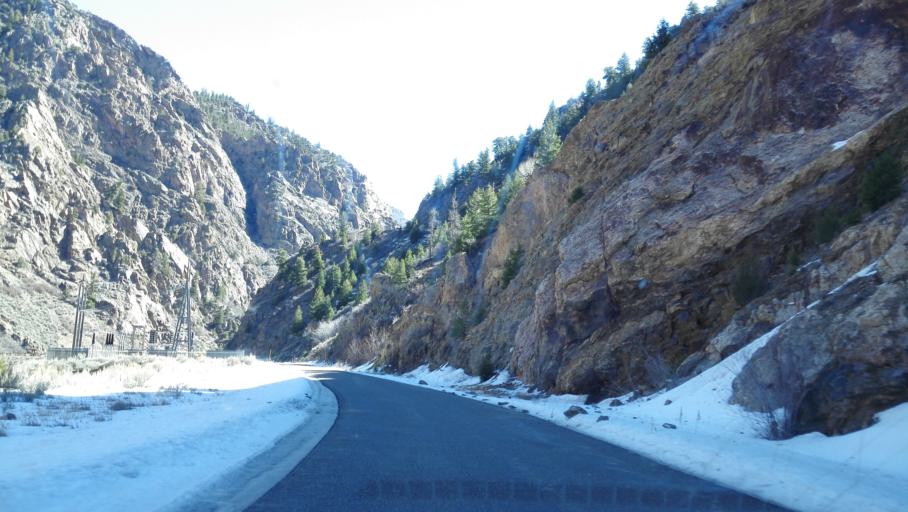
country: US
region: Colorado
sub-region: Montrose County
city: Montrose
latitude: 38.4516
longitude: -107.5470
